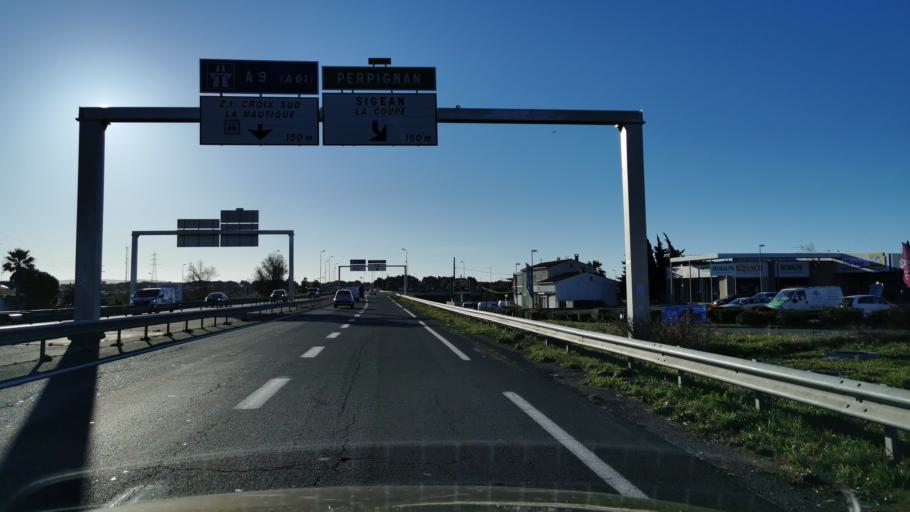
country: FR
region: Languedoc-Roussillon
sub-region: Departement de l'Aude
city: Narbonne
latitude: 43.1679
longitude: 2.9835
